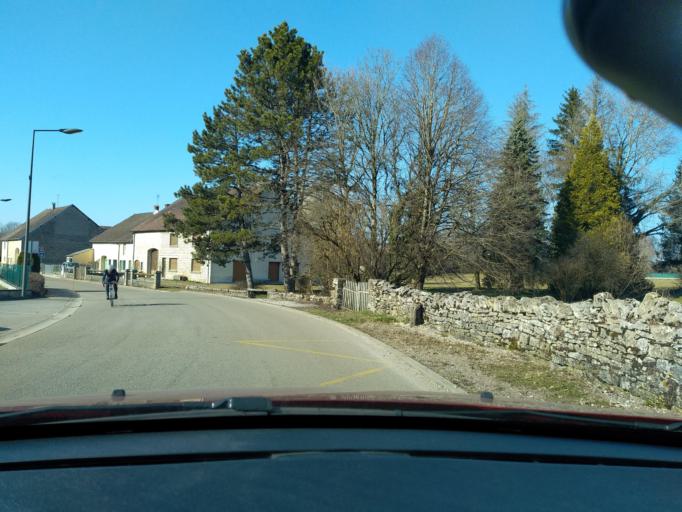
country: FR
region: Franche-Comte
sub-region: Departement du Jura
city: Perrigny
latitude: 46.6332
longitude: 5.6425
